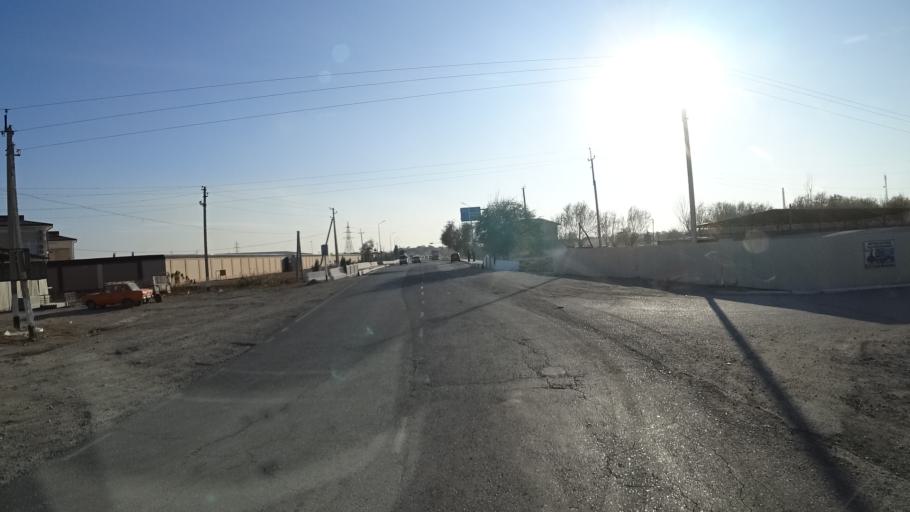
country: UZ
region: Navoiy
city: Beshrabot
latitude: 40.1665
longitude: 65.3323
